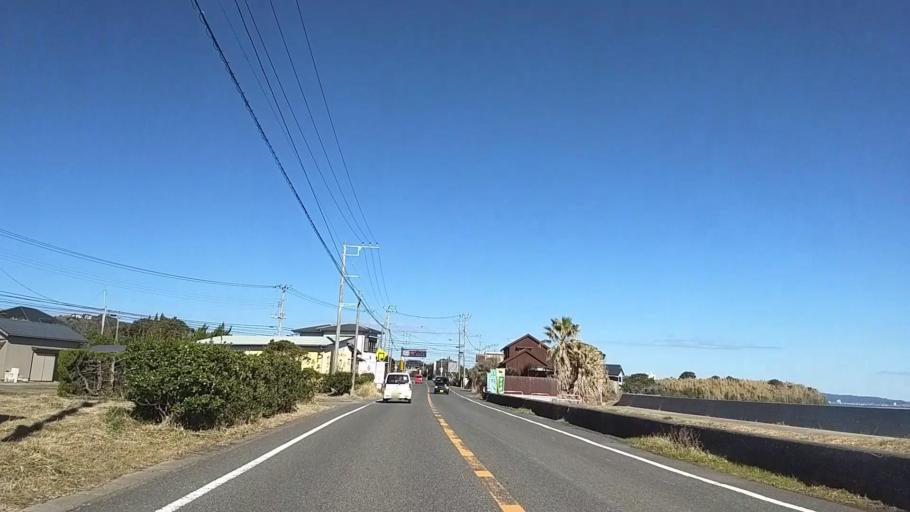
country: JP
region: Chiba
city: Tateyama
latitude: 34.9810
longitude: 139.9667
